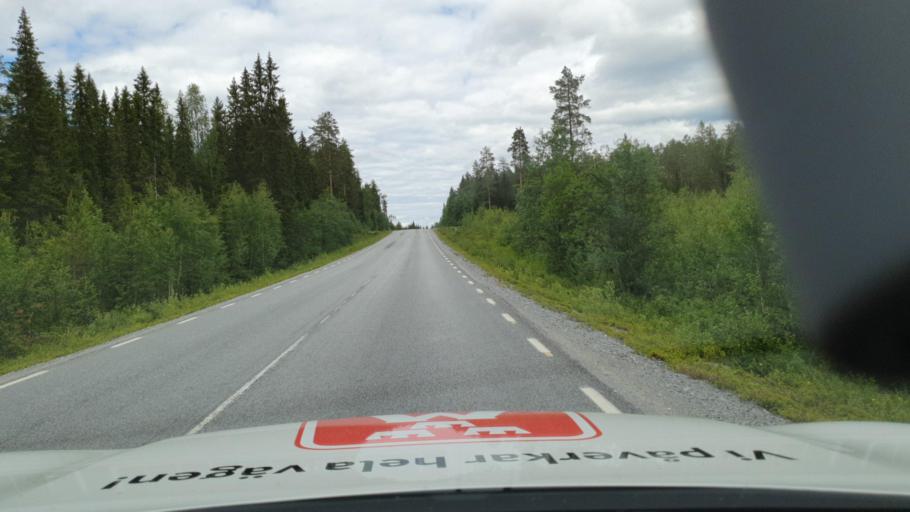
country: SE
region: Vaesterbotten
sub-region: Bjurholms Kommun
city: Bjurholm
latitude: 63.8902
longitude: 19.0630
